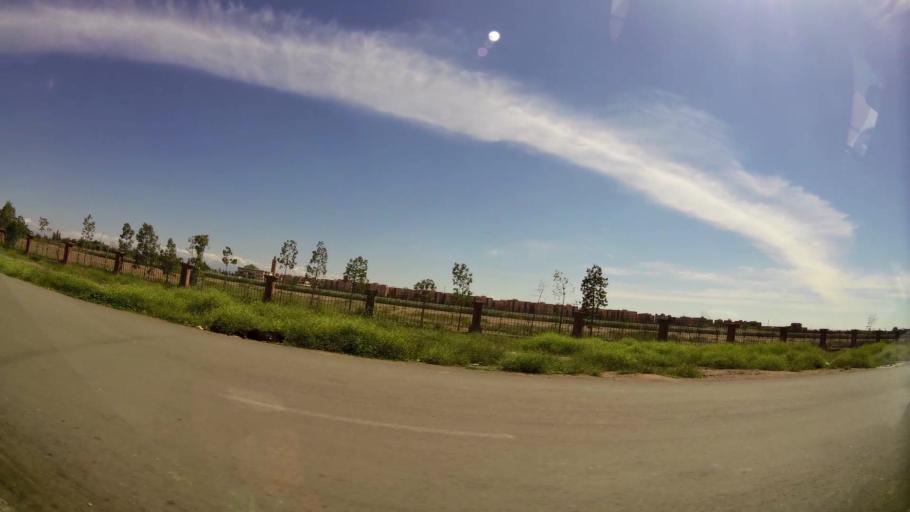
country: MA
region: Marrakech-Tensift-Al Haouz
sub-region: Marrakech
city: Marrakesh
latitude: 31.6402
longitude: -8.0959
